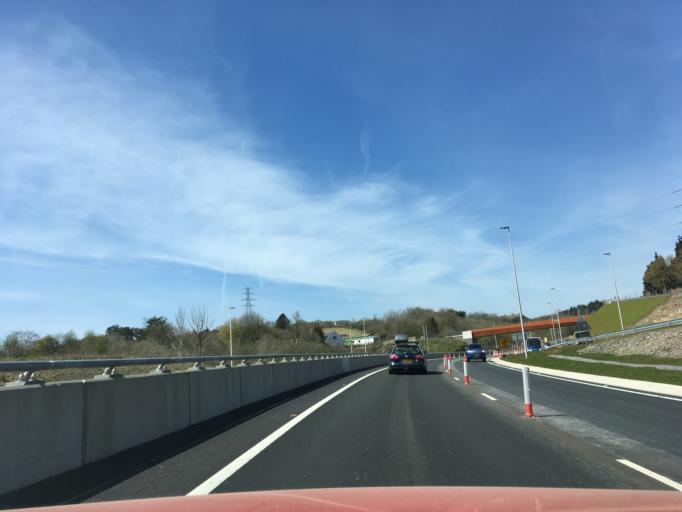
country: GB
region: Wales
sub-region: Blaenau Gwent
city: Brynmawr
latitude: 51.8031
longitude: -3.1660
